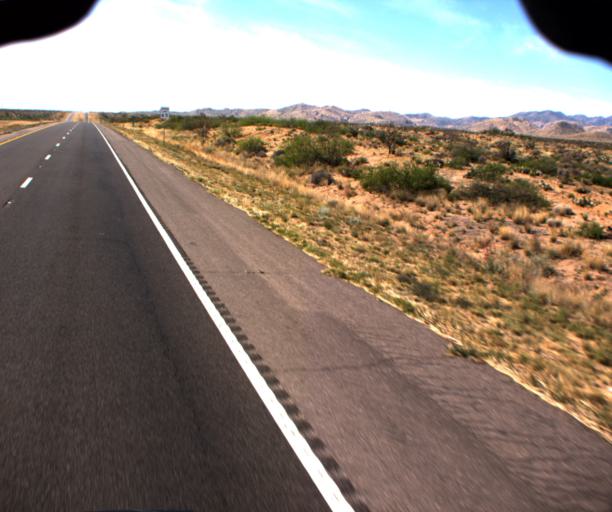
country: US
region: Arizona
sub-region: Graham County
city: Swift Trail Junction
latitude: 32.5935
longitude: -109.6847
